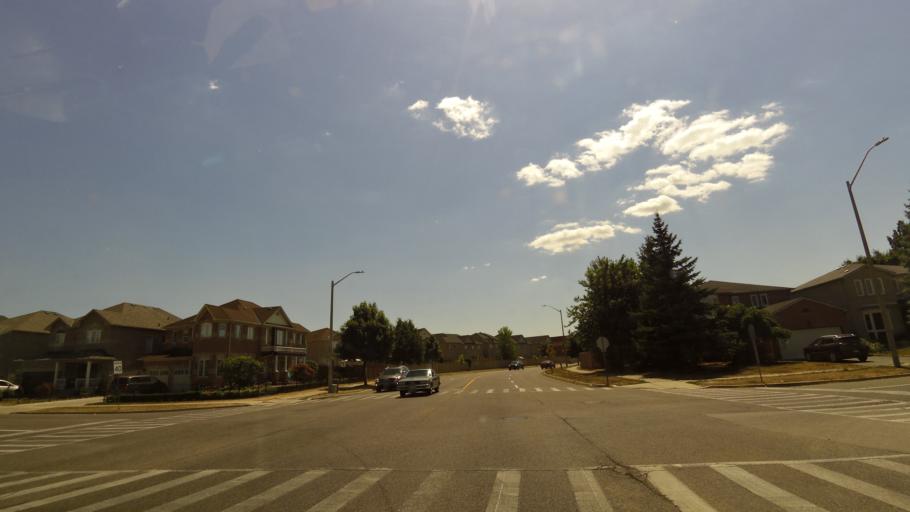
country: CA
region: Ontario
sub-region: Halton
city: Milton
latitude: 43.6344
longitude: -79.8767
